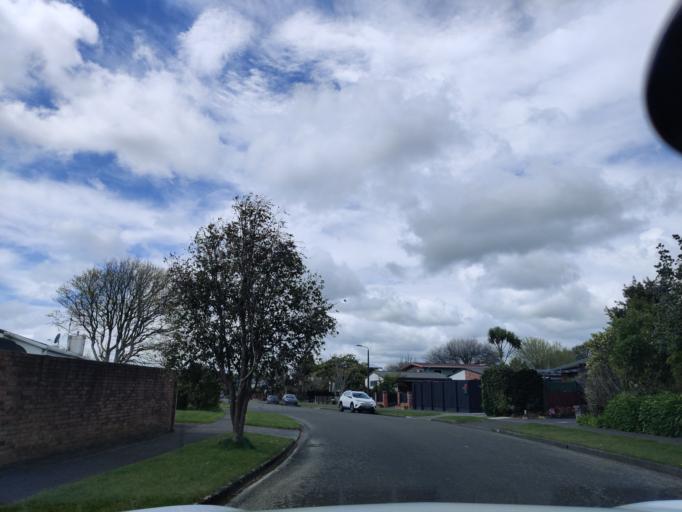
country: NZ
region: Manawatu-Wanganui
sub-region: Palmerston North City
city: Palmerston North
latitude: -40.3806
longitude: 175.5946
